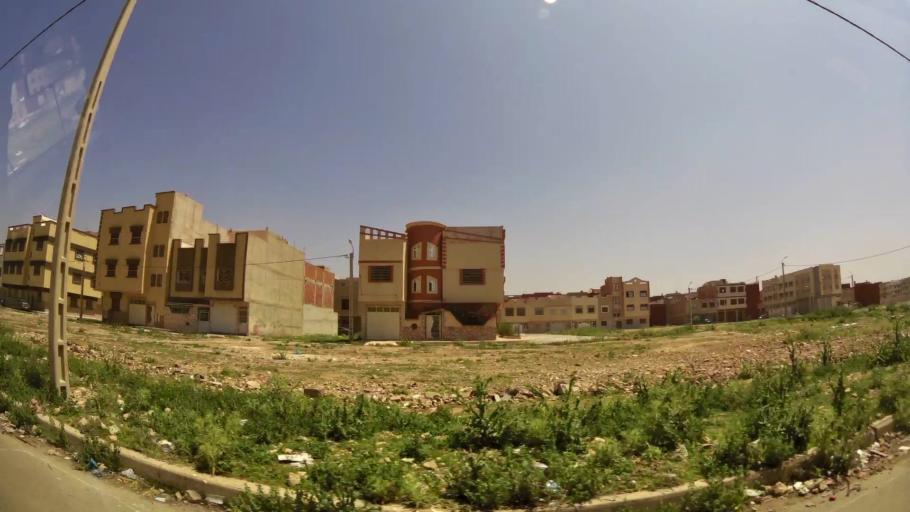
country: MA
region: Oriental
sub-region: Oujda-Angad
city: Oujda
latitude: 34.7001
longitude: -1.8868
